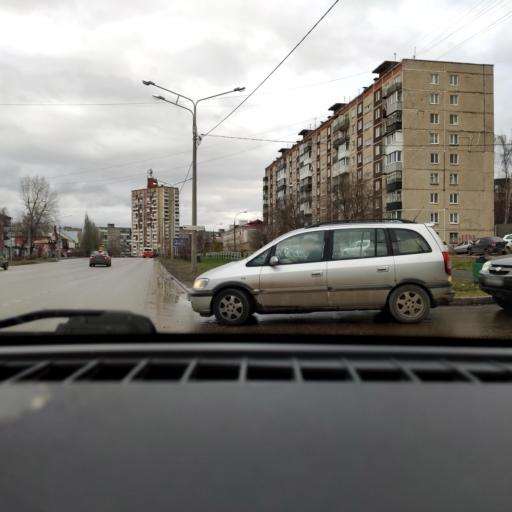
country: RU
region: Perm
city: Perm
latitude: 57.9752
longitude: 56.2112
